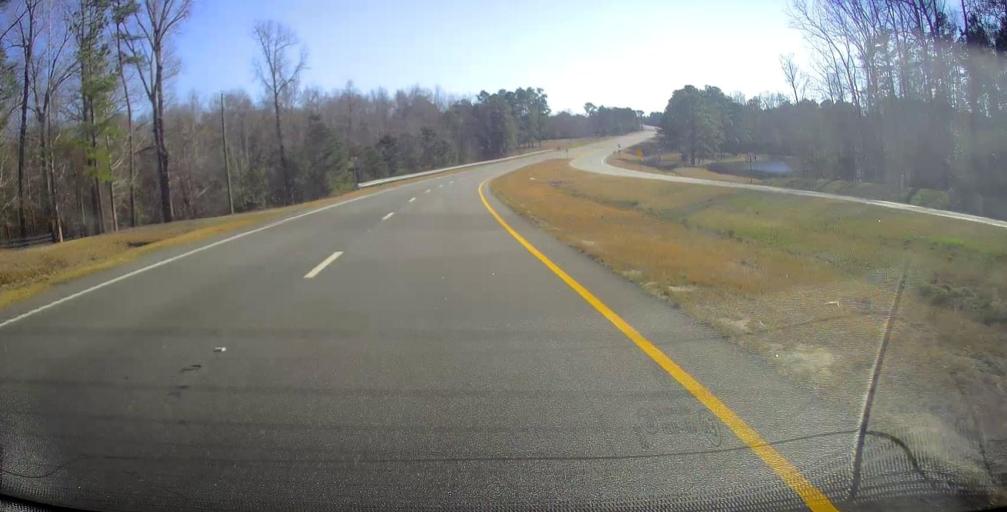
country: US
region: Georgia
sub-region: Taylor County
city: Butler
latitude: 32.5870
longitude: -84.2356
